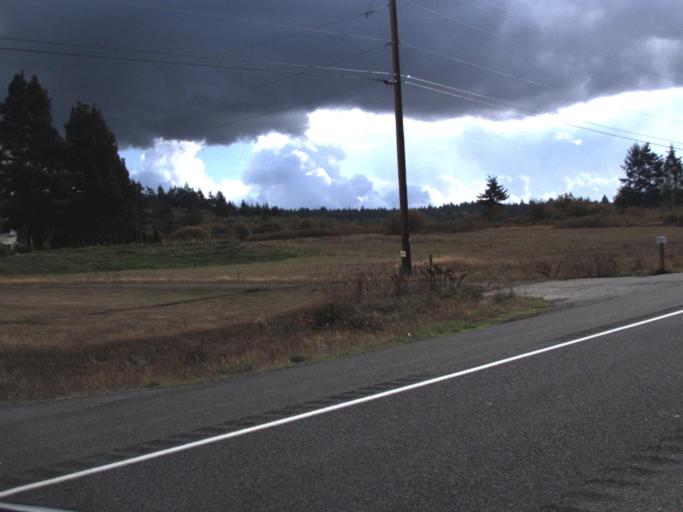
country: US
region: Washington
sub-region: Island County
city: Ault Field
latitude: 48.3825
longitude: -122.6503
